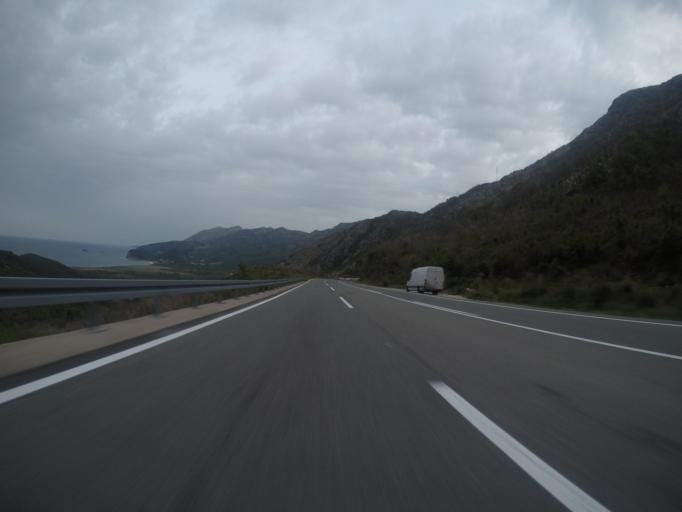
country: ME
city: Petrovac na Moru
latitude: 42.1782
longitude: 18.9967
